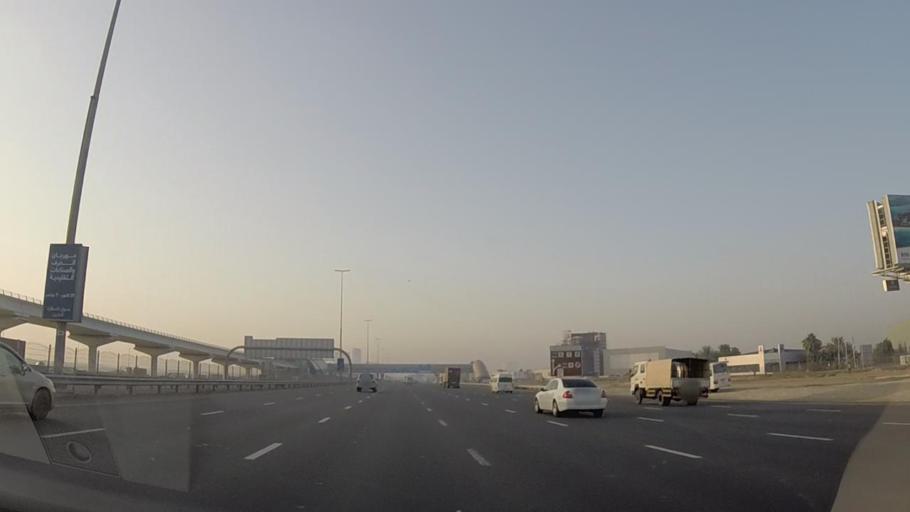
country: AE
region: Dubai
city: Dubai
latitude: 25.0046
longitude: 55.0956
